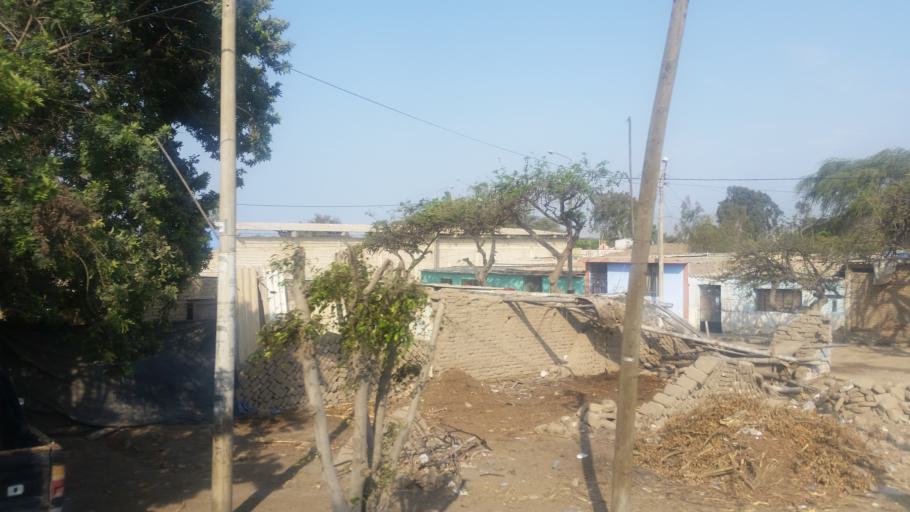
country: PE
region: Lambayeque
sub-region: Provincia de Chiclayo
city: Mocupe
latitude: -6.9920
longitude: -79.6199
